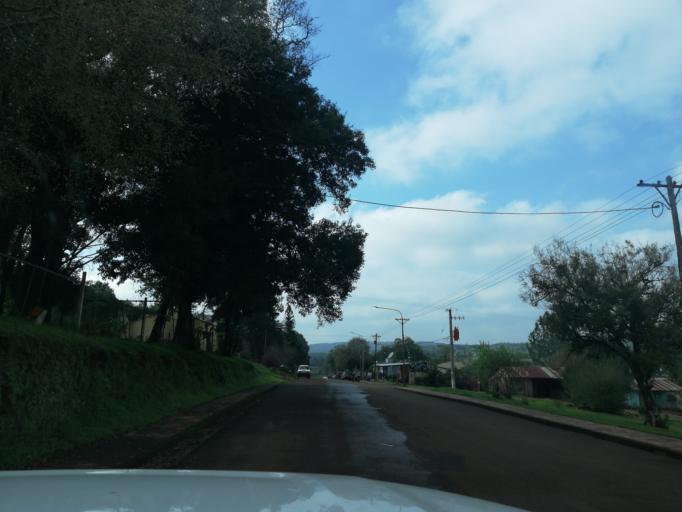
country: AR
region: Misiones
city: Cerro Azul
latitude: -27.5680
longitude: -55.5026
